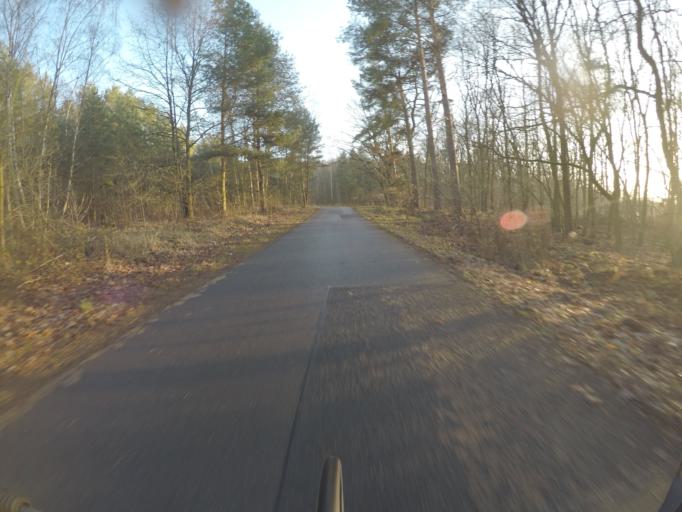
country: DE
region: Brandenburg
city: Hennigsdorf
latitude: 52.6489
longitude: 13.2269
